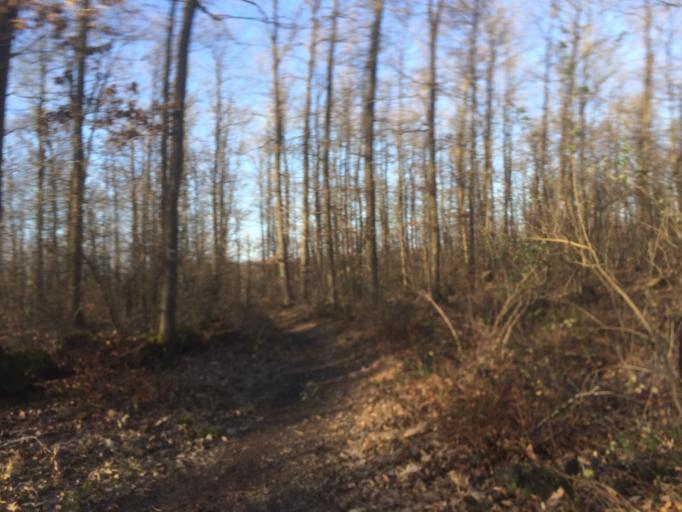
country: FR
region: Ile-de-France
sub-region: Departement de l'Essonne
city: Igny
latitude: 48.7413
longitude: 2.2195
